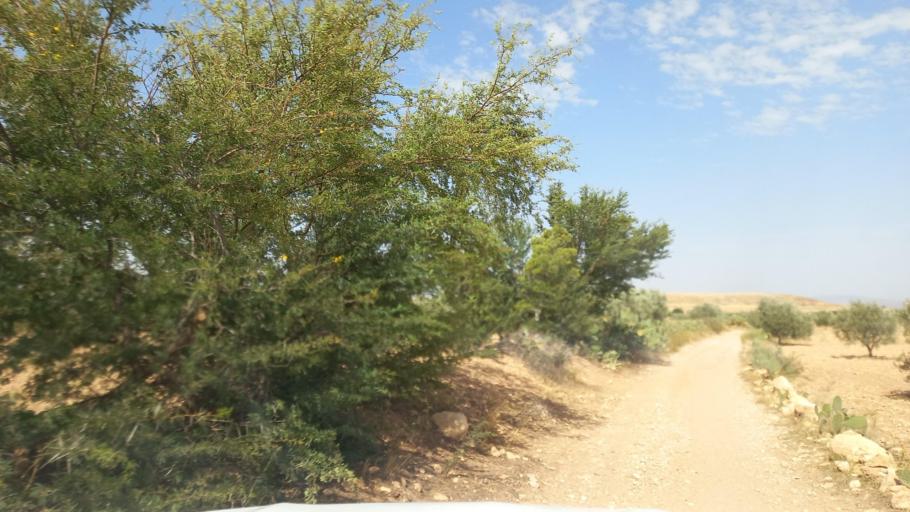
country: TN
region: Al Qasrayn
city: Kasserine
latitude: 35.2587
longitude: 8.9511
